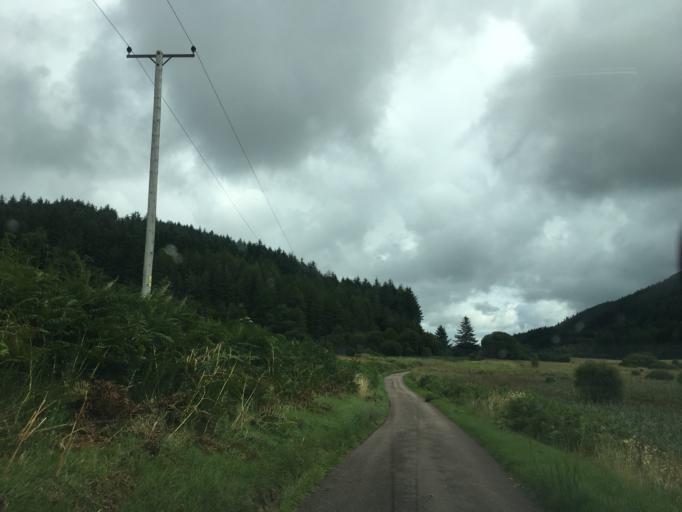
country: GB
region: Scotland
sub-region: Argyll and Bute
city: Oban
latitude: 56.2634
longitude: -5.3859
